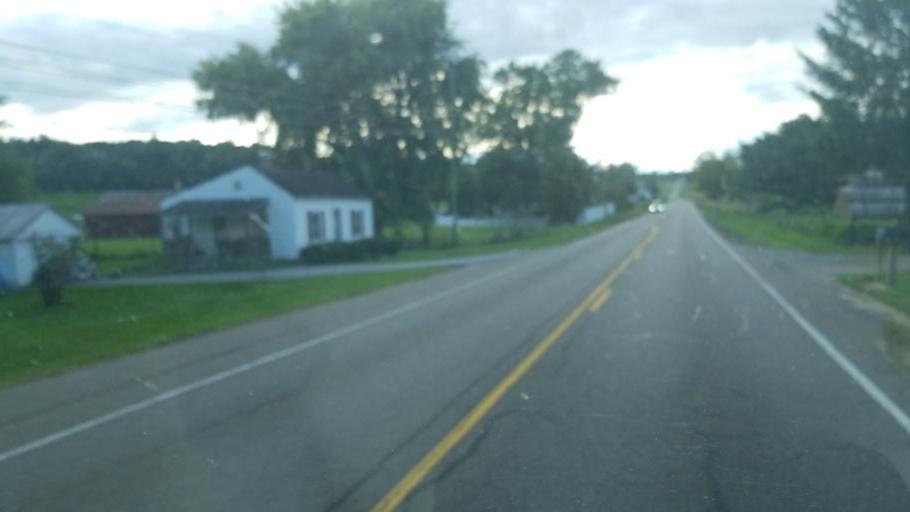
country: US
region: Ohio
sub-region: Knox County
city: Gambier
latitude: 40.4103
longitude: -82.3709
